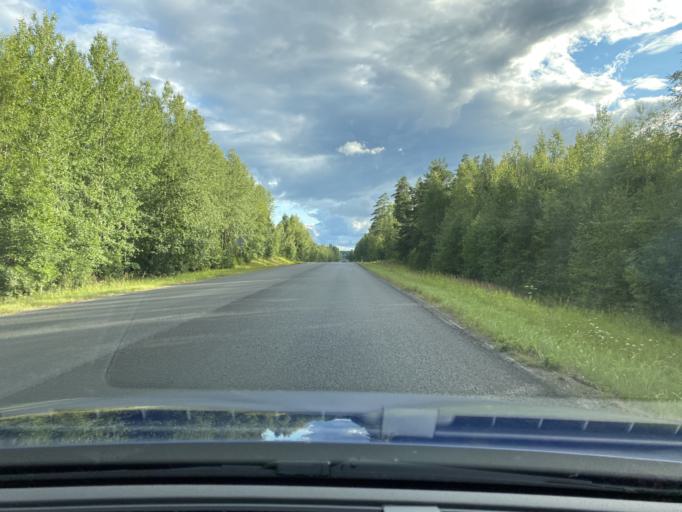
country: FI
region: Haeme
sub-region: Haemeenlinna
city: Renko
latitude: 60.9362
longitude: 24.3724
